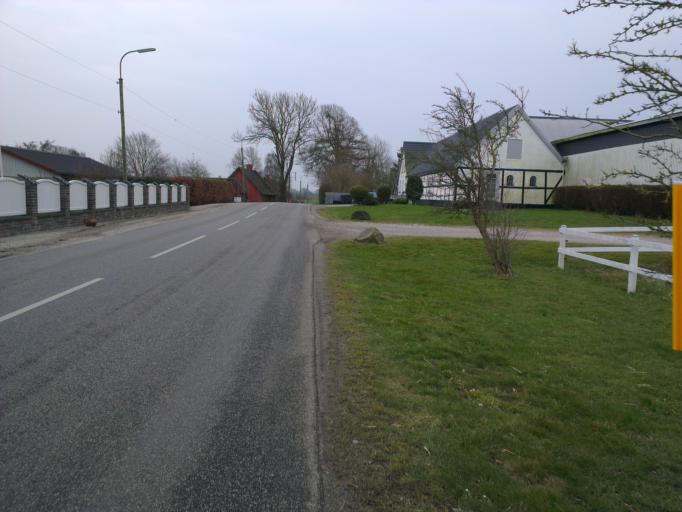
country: DK
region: Capital Region
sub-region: Frederikssund Kommune
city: Skibby
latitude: 55.7503
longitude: 11.9198
